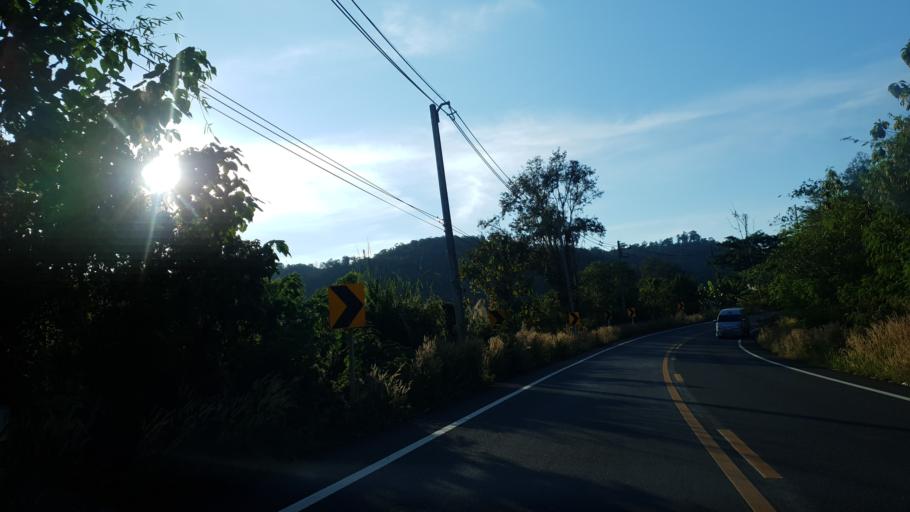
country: TH
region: Loei
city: Dan Sai
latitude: 17.2241
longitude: 101.0673
